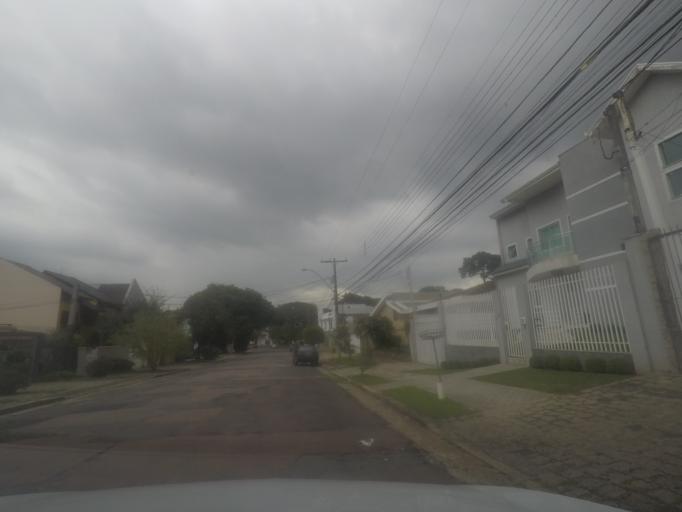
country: BR
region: Parana
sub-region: Curitiba
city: Curitiba
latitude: -25.4487
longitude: -49.3078
